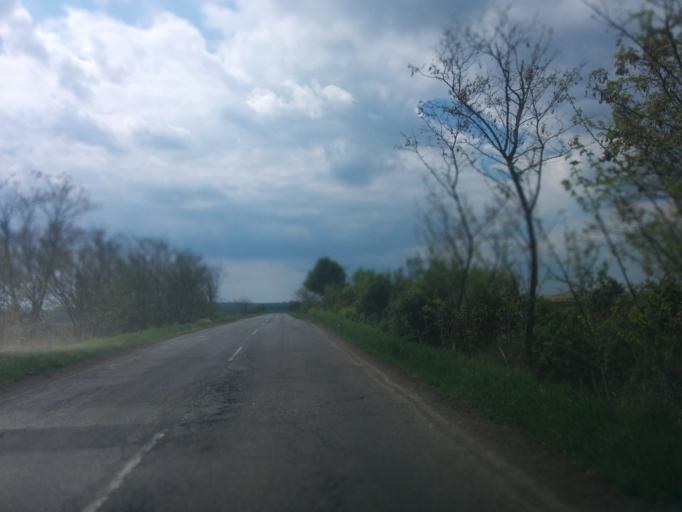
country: HU
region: Nograd
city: Jobbagyi
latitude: 47.8289
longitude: 19.6569
